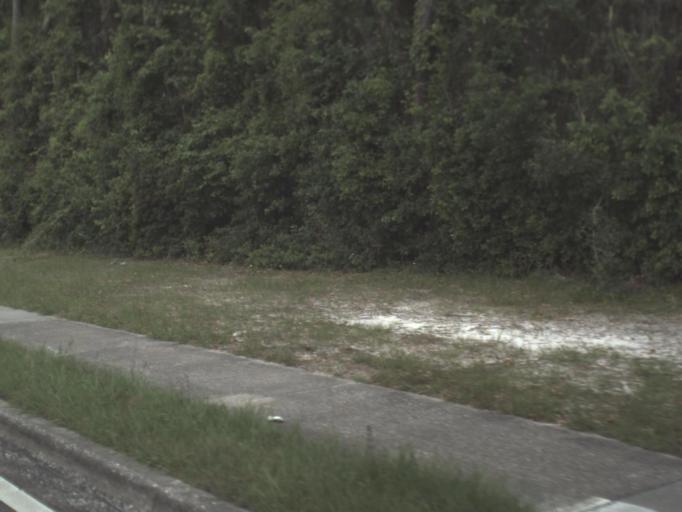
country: US
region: Florida
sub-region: Columbia County
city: Lake City
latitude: 30.1646
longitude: -82.6382
